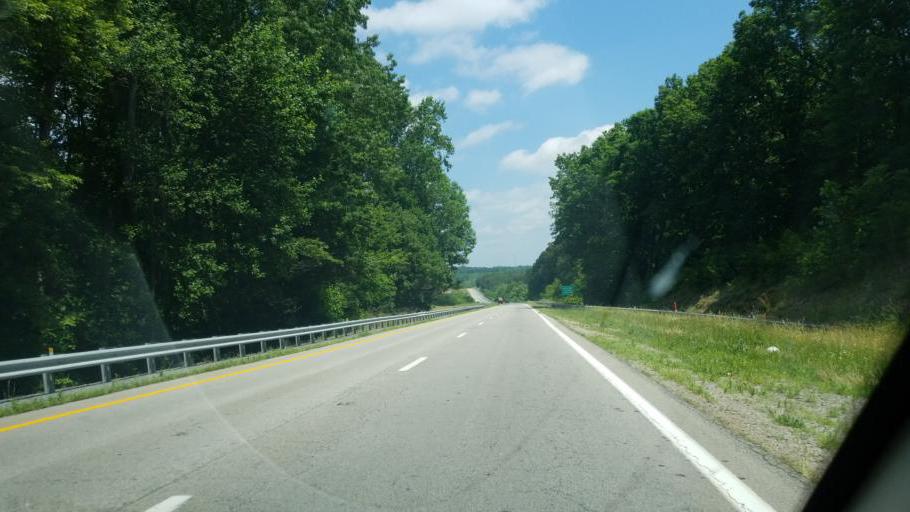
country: US
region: Virginia
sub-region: Pittsylvania County
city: Motley
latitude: 37.0894
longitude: -79.3318
